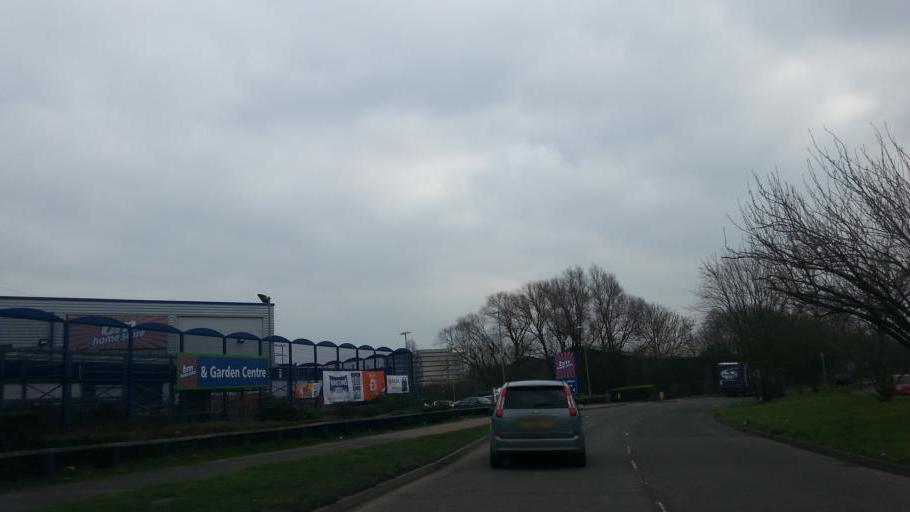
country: GB
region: England
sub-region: Northamptonshire
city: Corby
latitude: 52.4930
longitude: -0.6802
